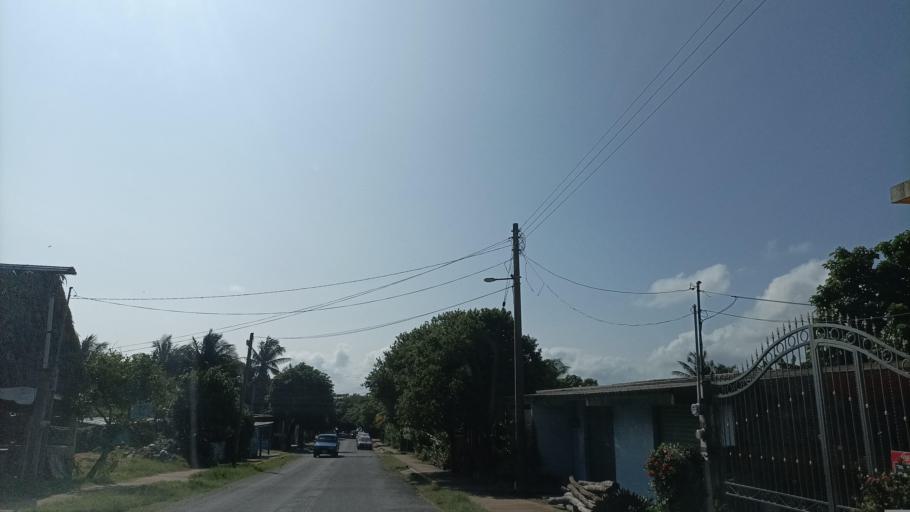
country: MX
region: Veracruz
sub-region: Coatzacoalcos
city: Fraccionamiento Ciudad Olmeca
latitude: 18.2128
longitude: -94.6129
